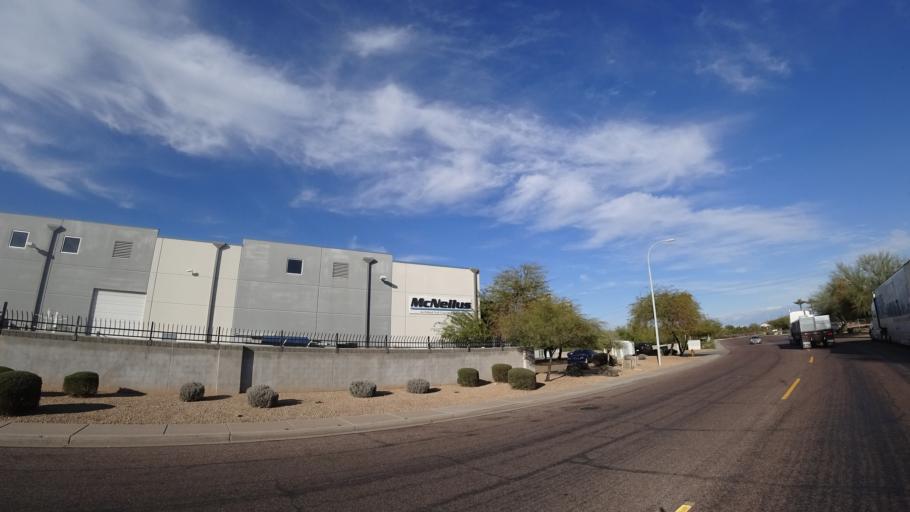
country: US
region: Arizona
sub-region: Maricopa County
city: Glendale
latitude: 33.4612
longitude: -112.1619
